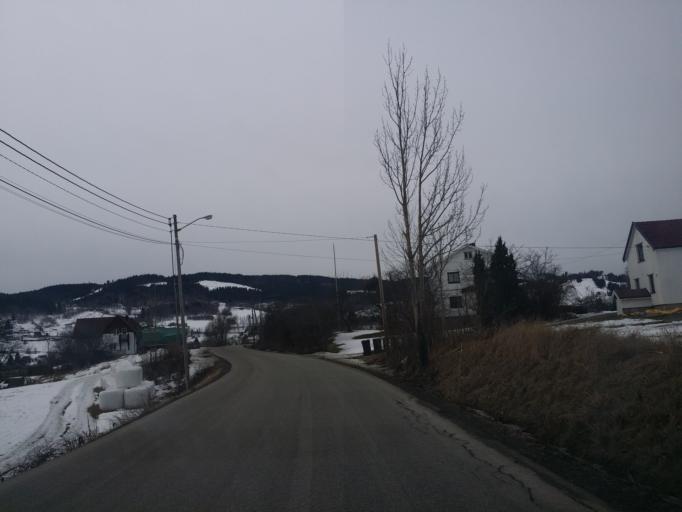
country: NO
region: Buskerud
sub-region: Lier
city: Tranby
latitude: 59.8562
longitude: 10.2335
